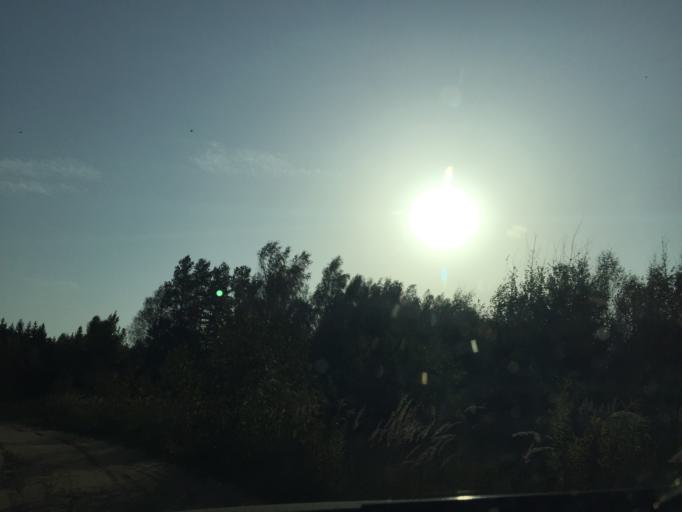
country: LV
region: Garkalne
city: Garkalne
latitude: 56.9726
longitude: 24.4175
